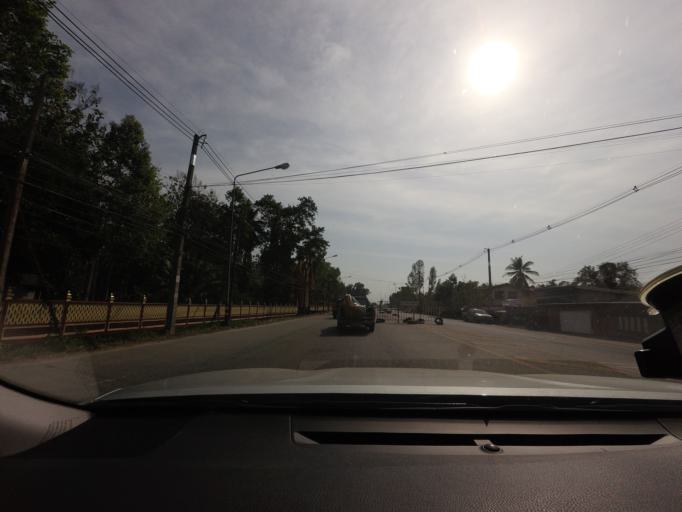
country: TH
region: Narathiwat
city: Narathiwat
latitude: 6.3793
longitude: 101.8021
